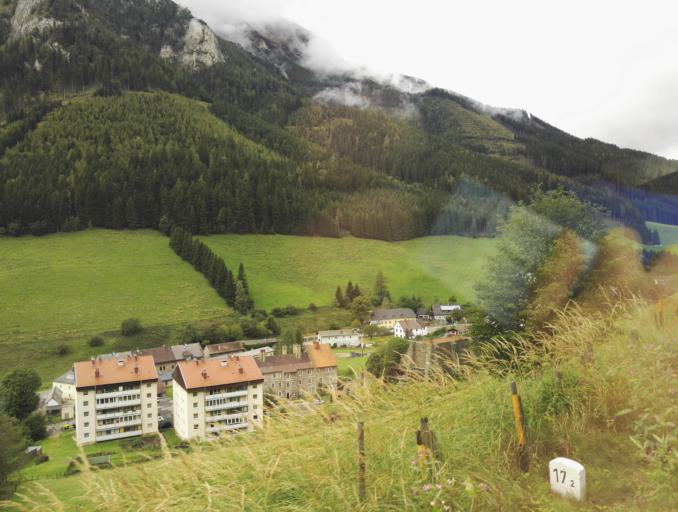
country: AT
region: Styria
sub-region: Politischer Bezirk Leoben
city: Vordernberg
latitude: 47.4932
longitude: 14.9955
